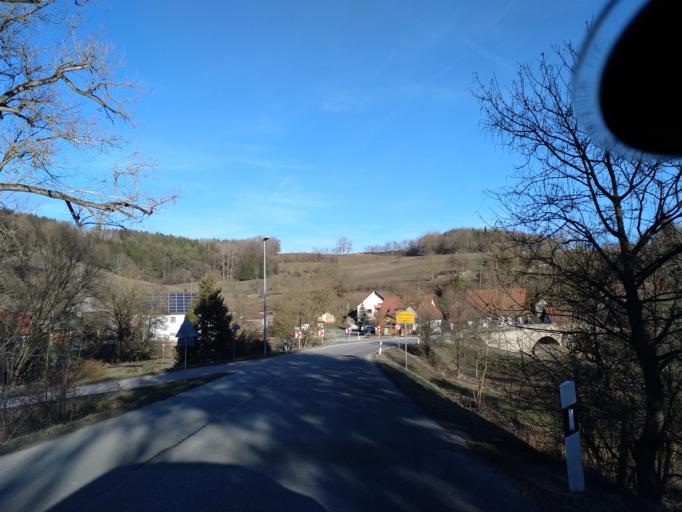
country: DE
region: Baden-Wuerttemberg
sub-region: Regierungsbezirk Stuttgart
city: Vellberg
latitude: 49.0834
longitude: 9.8934
